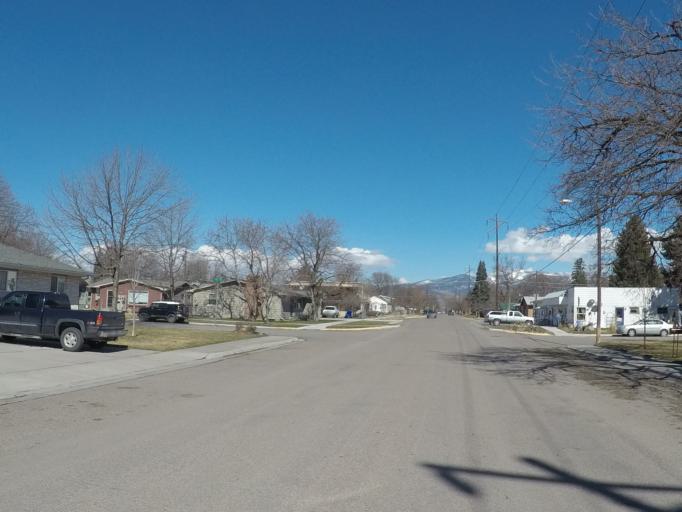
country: US
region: Montana
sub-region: Missoula County
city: Orchard Homes
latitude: 46.8581
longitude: -114.0224
